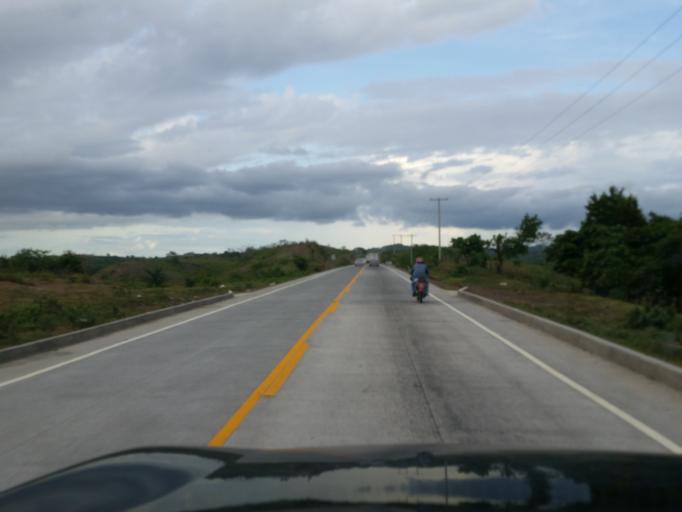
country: NI
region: Managua
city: Carlos Fonseca Amador
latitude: 12.0687
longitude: -86.4408
